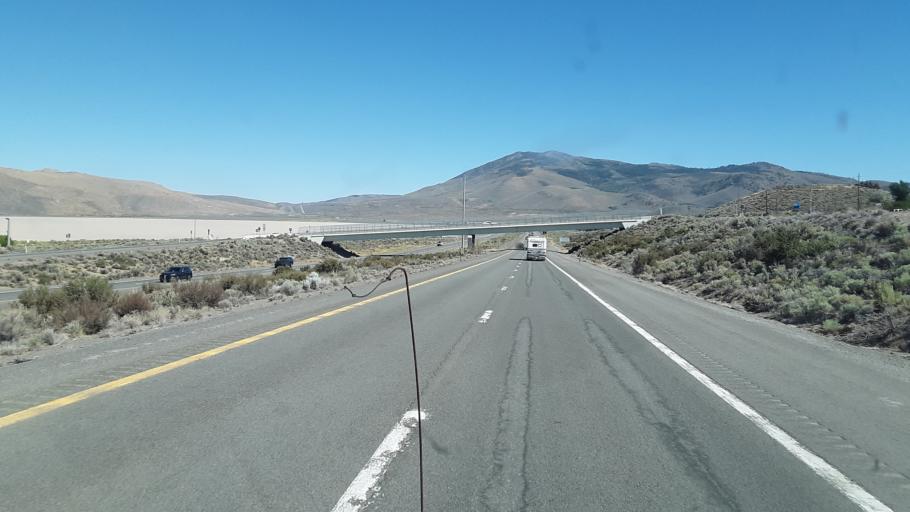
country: US
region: Nevada
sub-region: Washoe County
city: Cold Springs
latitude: 39.6697
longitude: -119.9981
